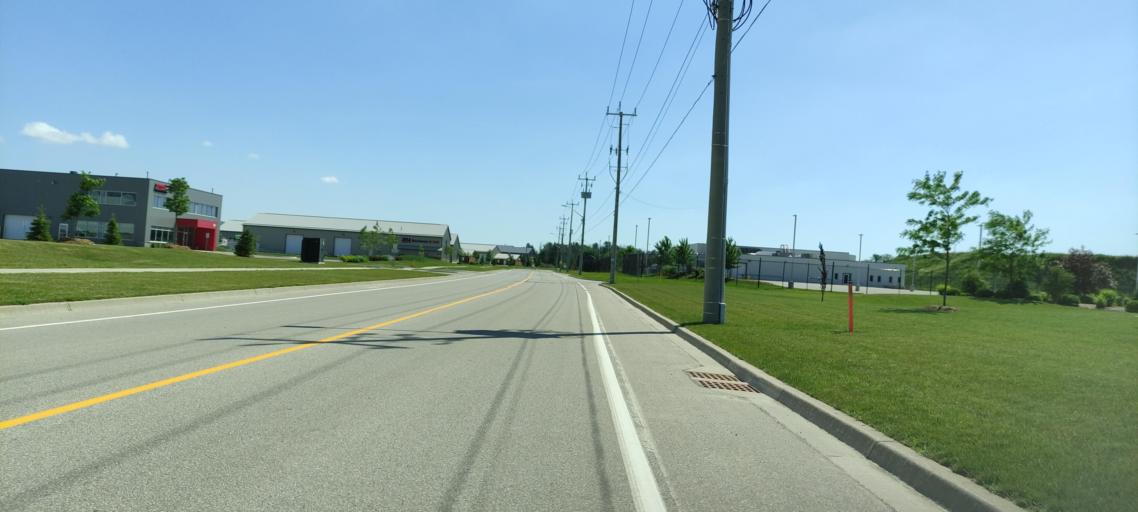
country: CA
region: Ontario
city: Stratford
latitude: 43.3491
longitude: -81.0165
